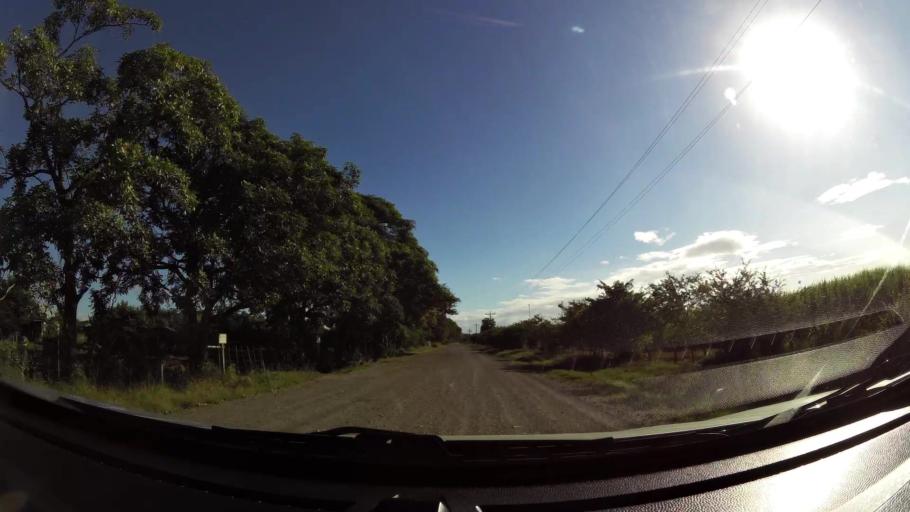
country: CR
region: Guanacaste
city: Belen
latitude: 10.4858
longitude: -85.5726
